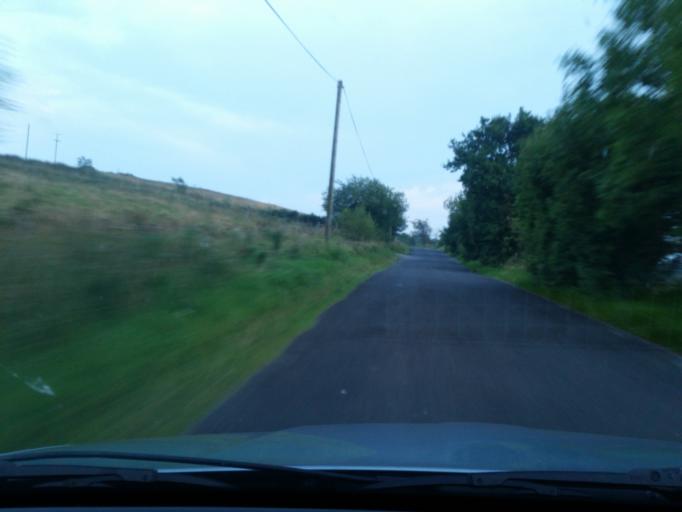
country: GB
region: Northern Ireland
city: Fivemiletown
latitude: 54.2860
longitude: -7.2763
